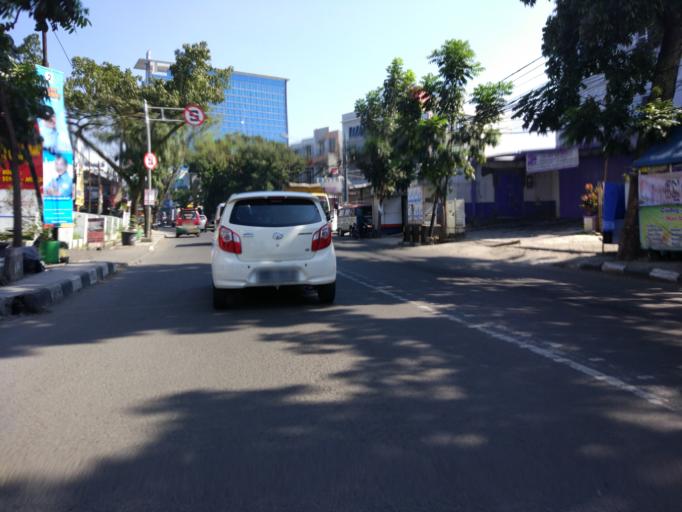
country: ID
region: West Java
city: Bandung
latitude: -6.9293
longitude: 107.6385
